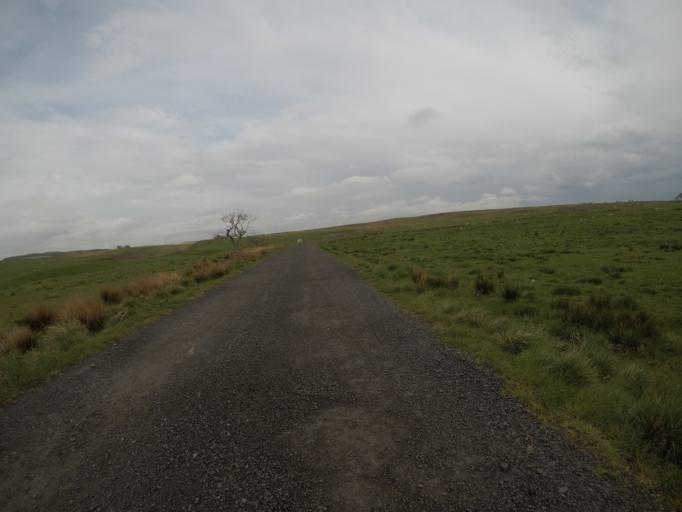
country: GB
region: Scotland
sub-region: East Ayrshire
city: Galston
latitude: 55.6856
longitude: -4.4071
